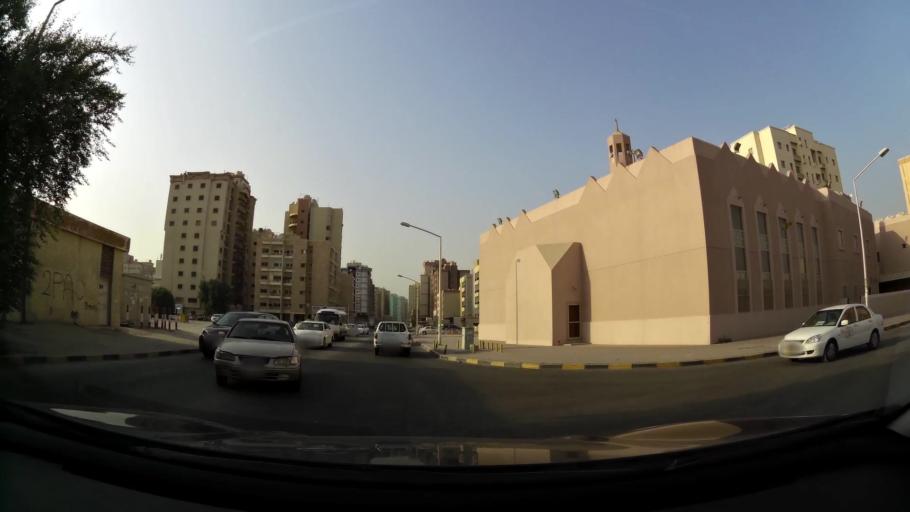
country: KW
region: Muhafazat Hawalli
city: As Salimiyah
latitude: 29.3266
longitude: 48.0636
